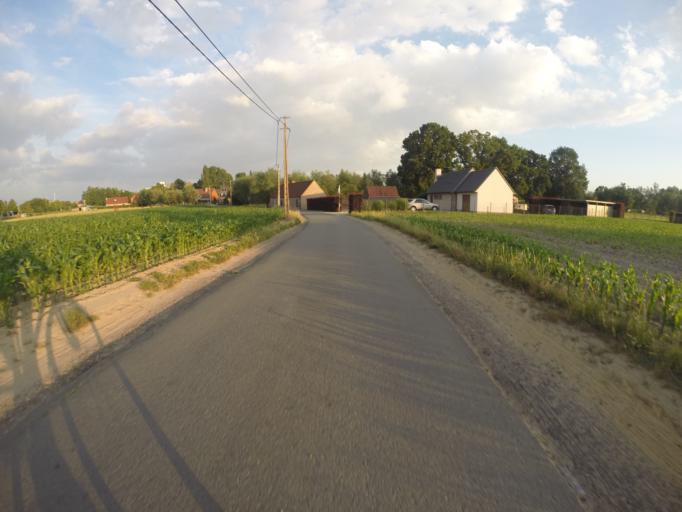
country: BE
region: Flanders
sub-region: Provincie West-Vlaanderen
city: Beernem
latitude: 51.1418
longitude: 3.3278
